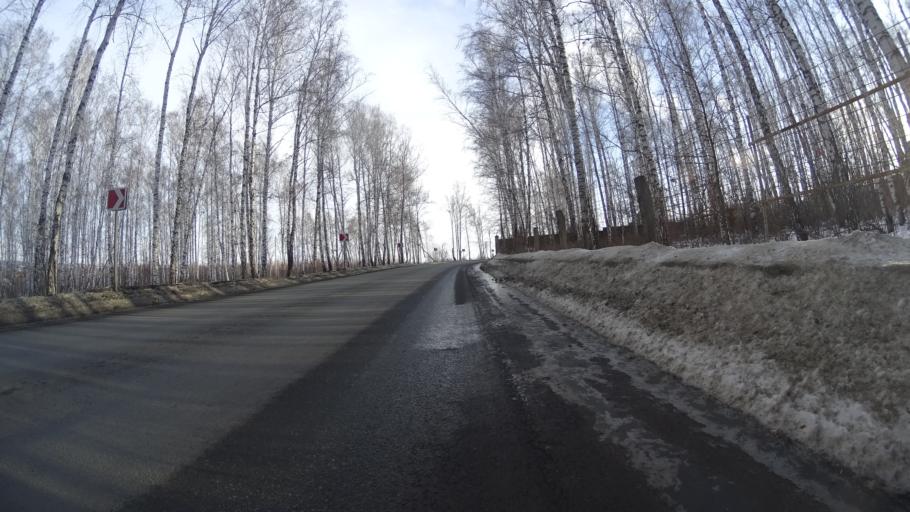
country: RU
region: Chelyabinsk
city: Sargazy
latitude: 55.1261
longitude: 61.2893
